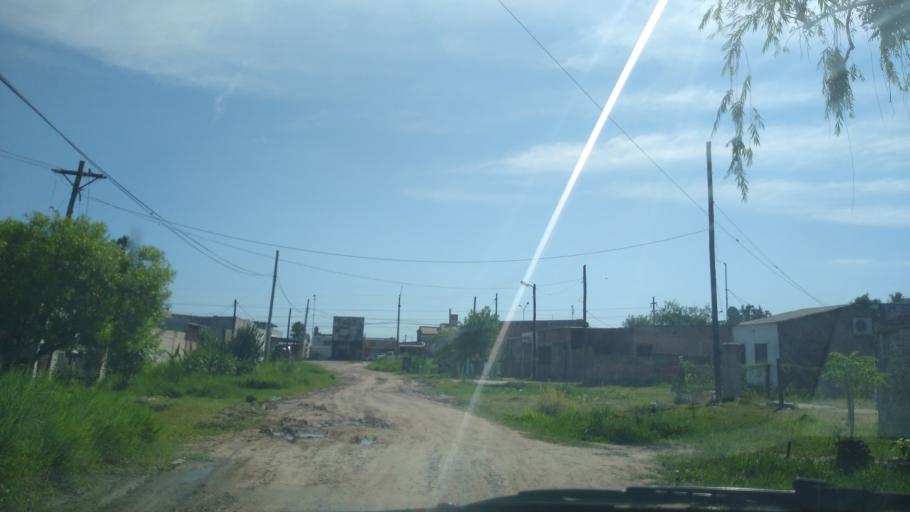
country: AR
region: Chaco
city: Barranqueras
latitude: -27.4897
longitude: -58.9559
